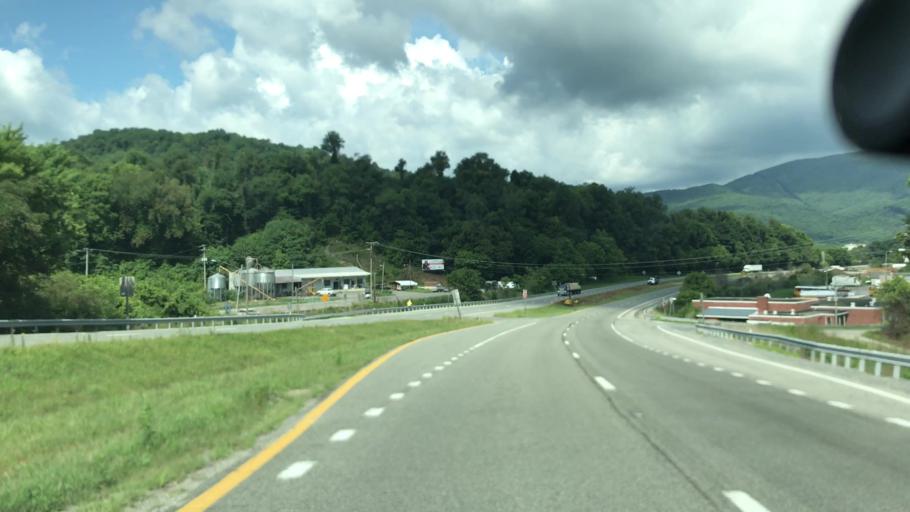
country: US
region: Virginia
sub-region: Giles County
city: Pearisburg
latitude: 37.3350
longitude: -80.7501
